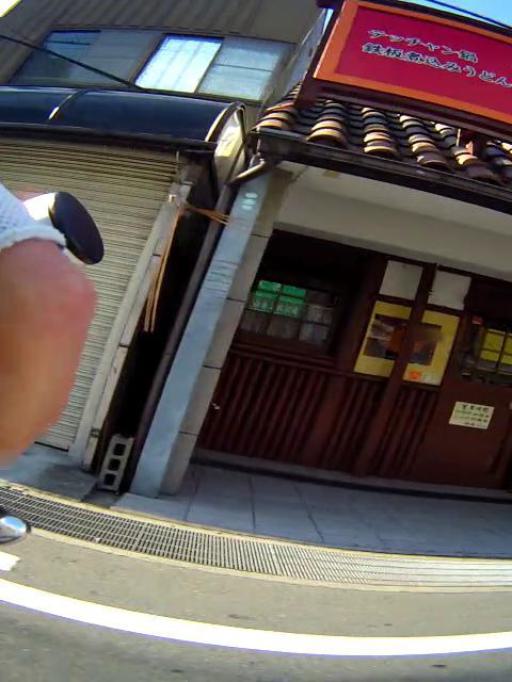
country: JP
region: Osaka
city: Daitocho
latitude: 34.6594
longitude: 135.6400
